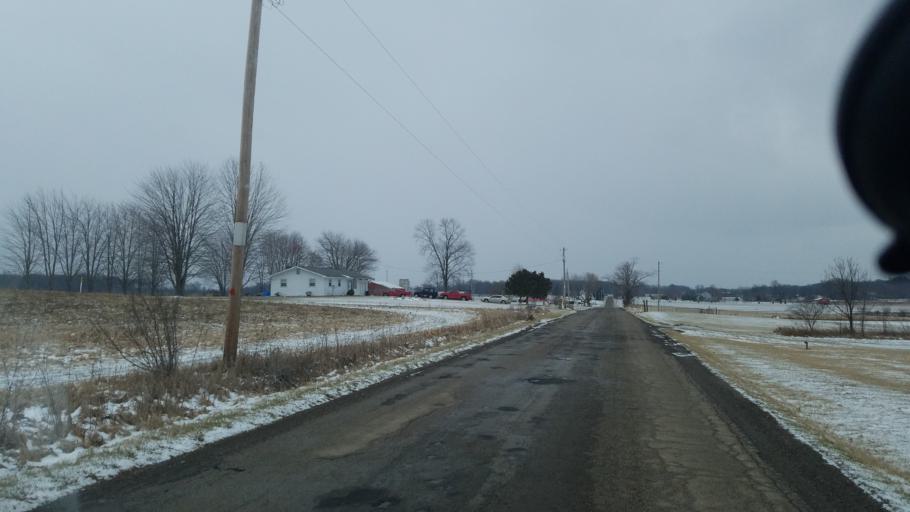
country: US
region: Ohio
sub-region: Morrow County
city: Mount Gilead
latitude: 40.4946
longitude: -82.8086
